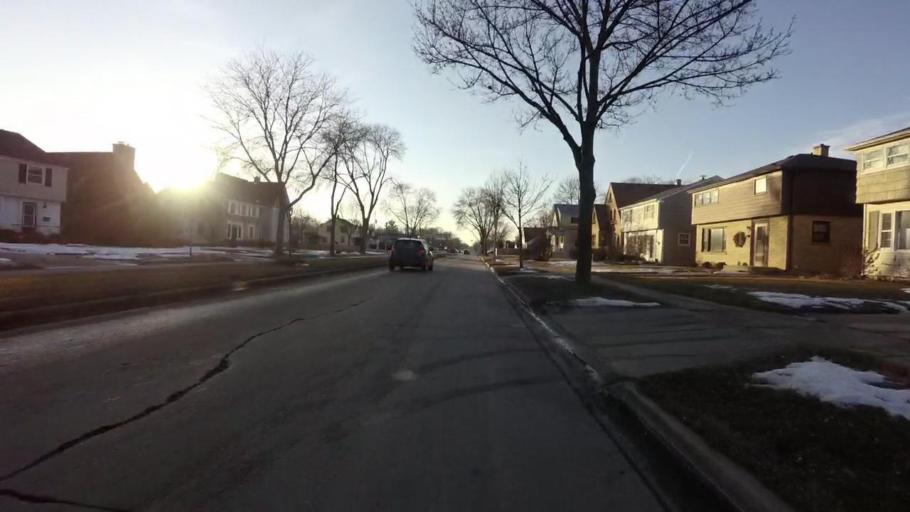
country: US
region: Wisconsin
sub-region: Milwaukee County
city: Whitefish Bay
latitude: 43.1040
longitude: -87.9041
